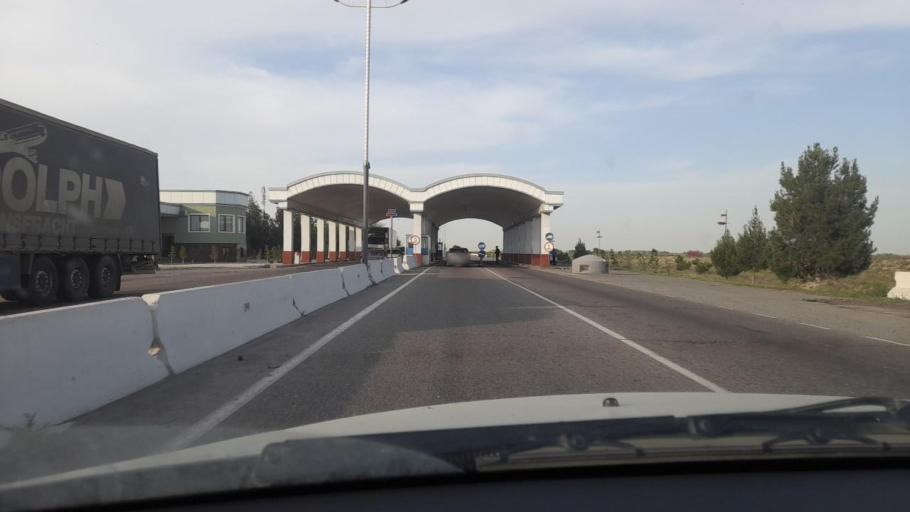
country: UZ
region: Jizzax
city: Dustlik
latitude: 40.4146
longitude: 68.2063
